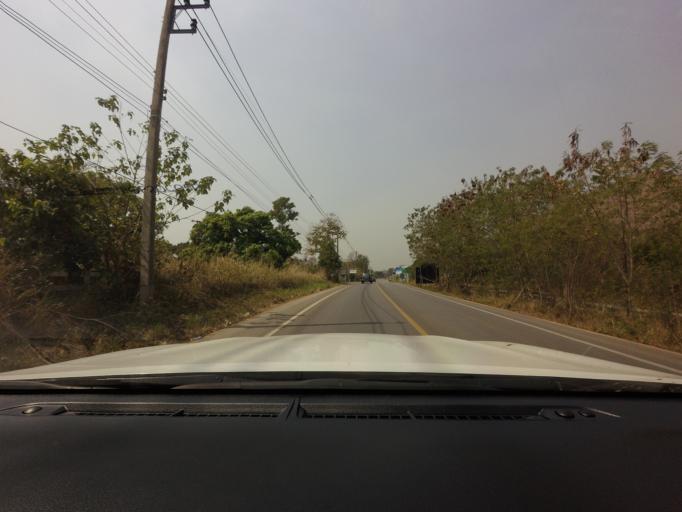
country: TH
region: Sara Buri
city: Muak Lek
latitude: 14.5886
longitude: 101.2354
